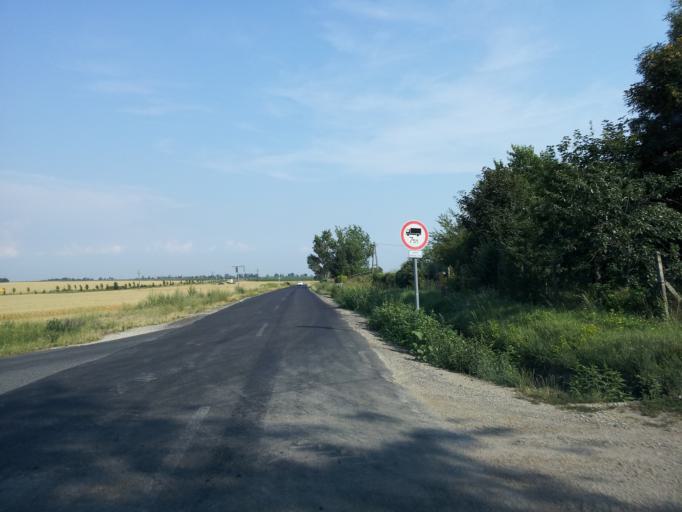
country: HU
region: Veszprem
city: Balatonkenese
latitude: 47.0725
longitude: 18.0700
